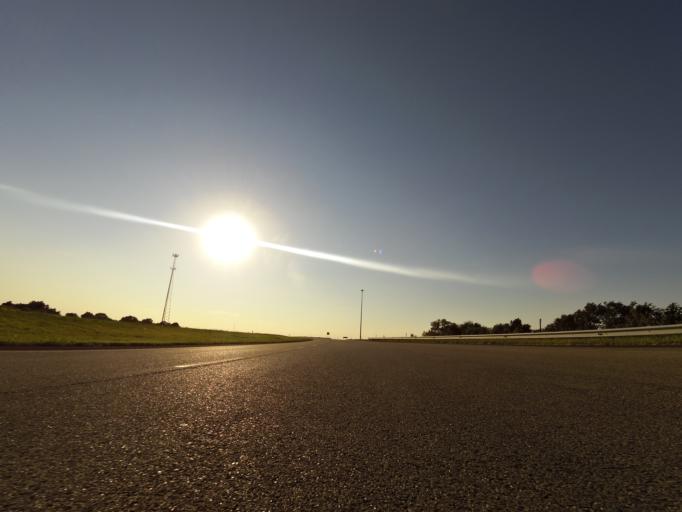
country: US
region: Kansas
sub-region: Reno County
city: Haven
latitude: 37.9352
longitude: -97.8607
